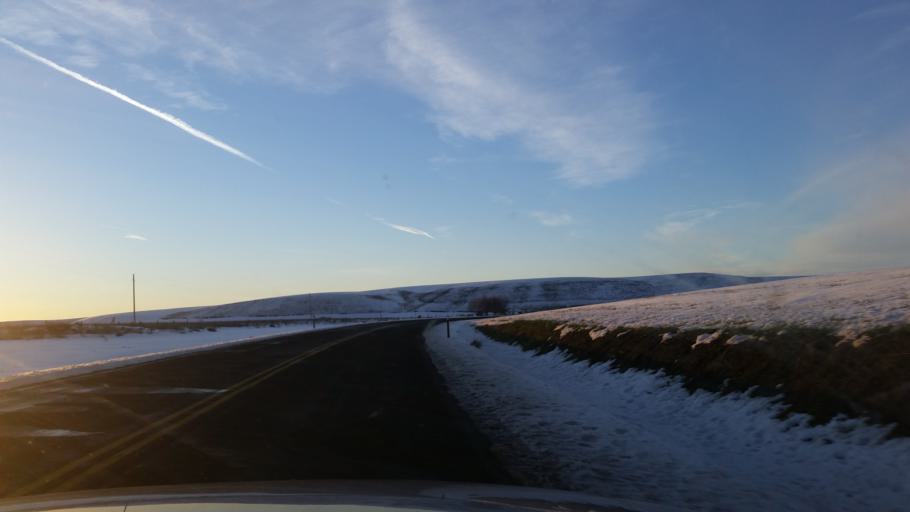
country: US
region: Washington
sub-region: Spokane County
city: Cheney
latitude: 47.1110
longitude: -117.8154
